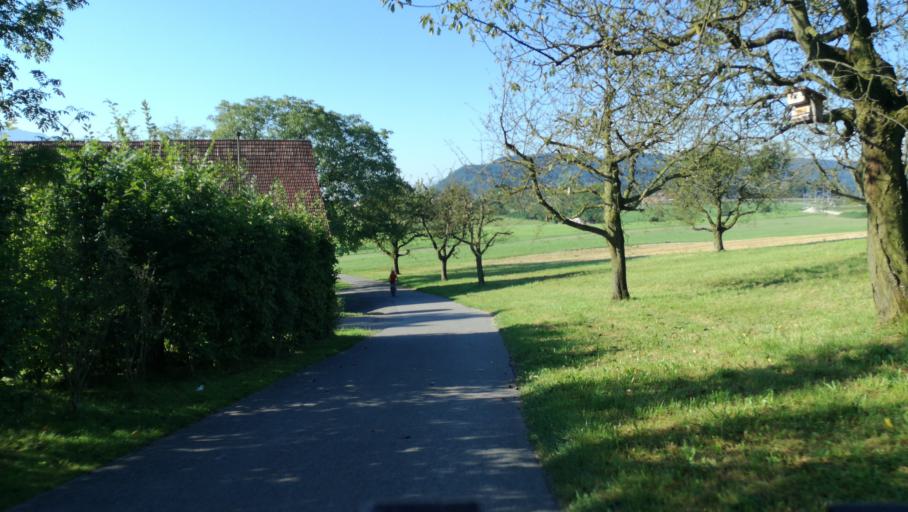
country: CH
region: Lucerne
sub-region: Lucerne-Land District
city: Meierskappel
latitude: 47.1497
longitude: 8.4548
